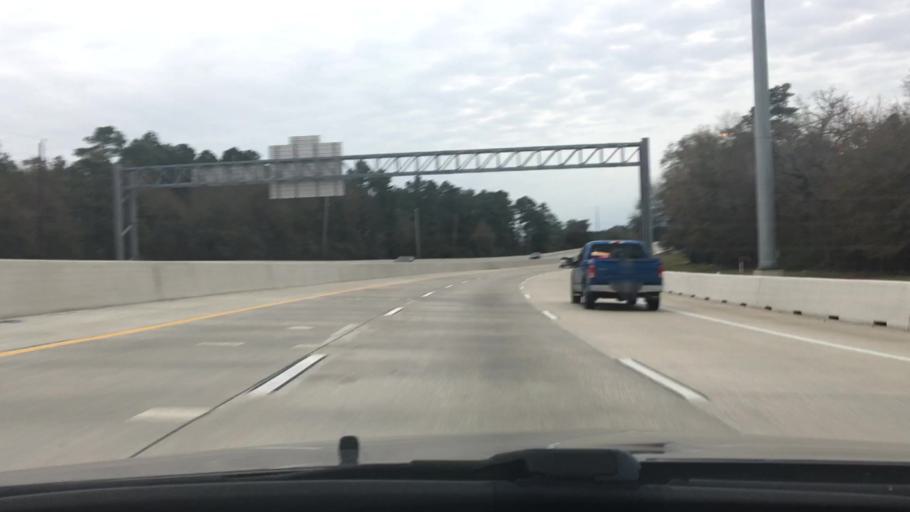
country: US
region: Texas
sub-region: Harris County
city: Spring
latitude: 30.0798
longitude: -95.4109
